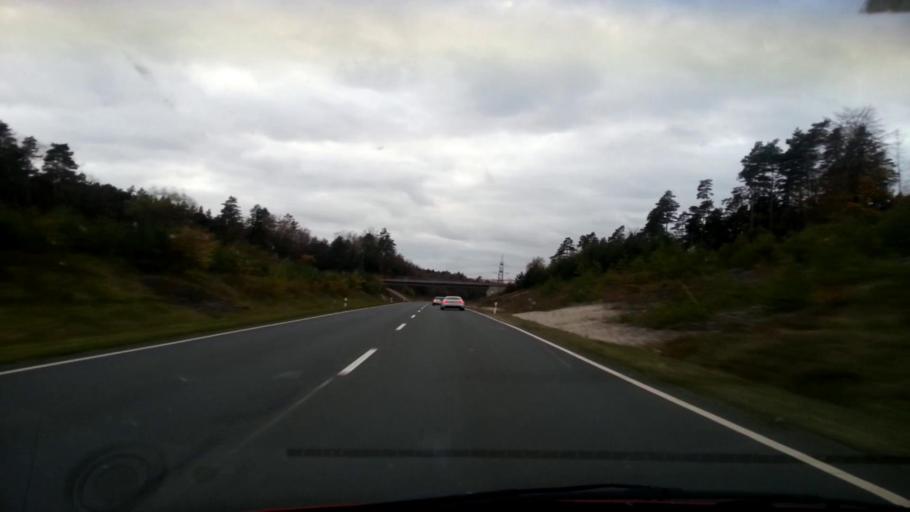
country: DE
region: Bavaria
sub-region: Upper Franconia
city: Schneckenlohe
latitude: 50.2088
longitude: 11.1695
